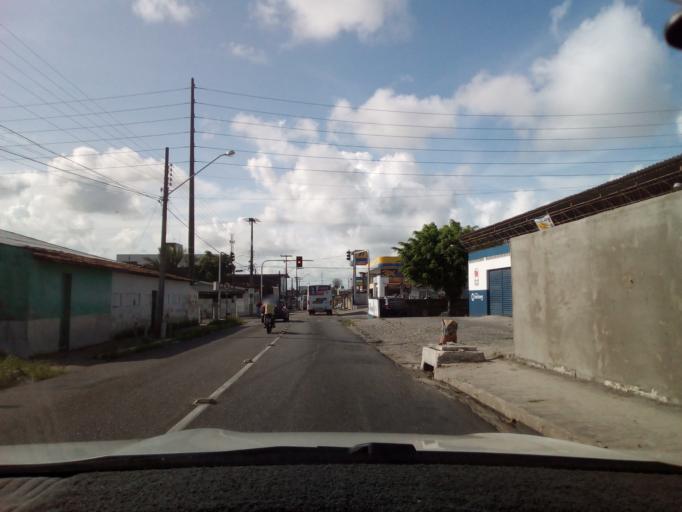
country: BR
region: Paraiba
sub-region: Joao Pessoa
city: Joao Pessoa
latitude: -7.1469
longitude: -34.8738
